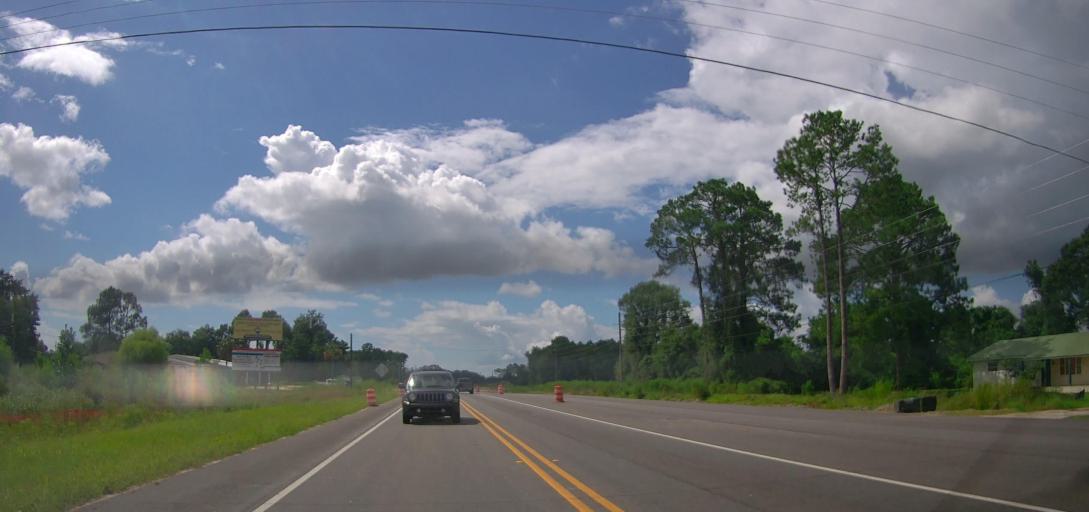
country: US
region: Georgia
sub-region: Coffee County
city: Douglas
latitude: 31.5444
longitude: -82.9325
